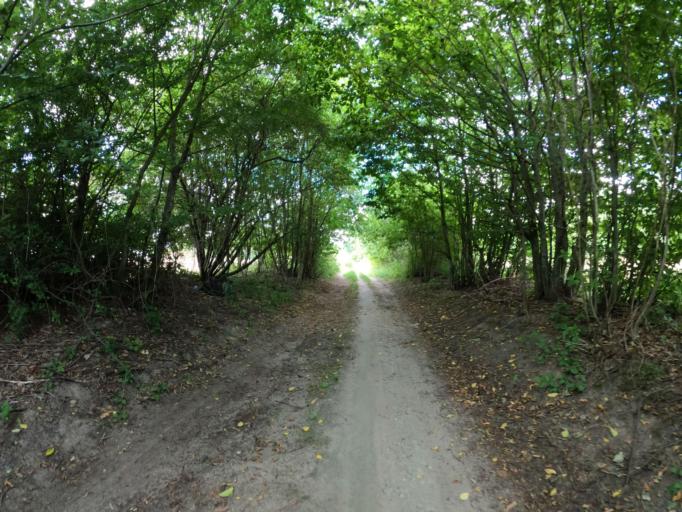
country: PL
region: West Pomeranian Voivodeship
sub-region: Powiat swidwinski
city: Swidwin
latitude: 53.7525
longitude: 15.8181
